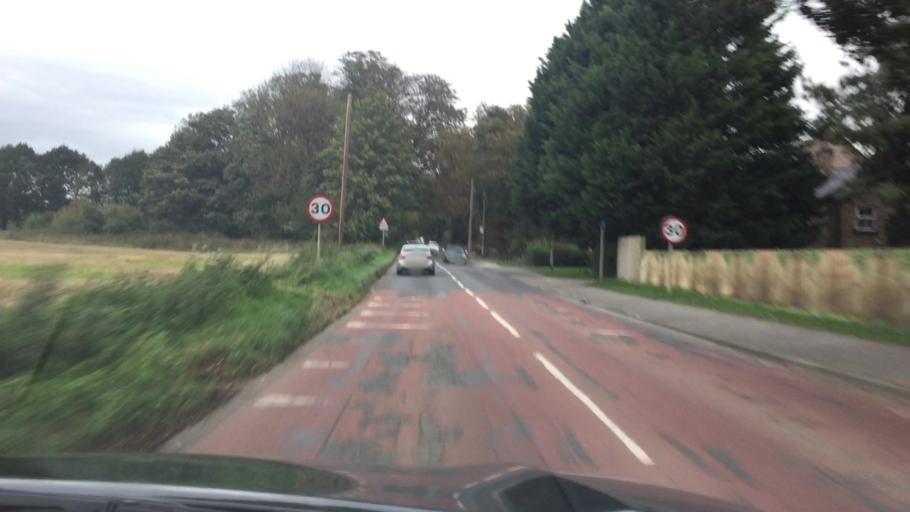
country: GB
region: England
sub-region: East Riding of Yorkshire
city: Pocklington
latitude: 53.9250
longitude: -0.7849
